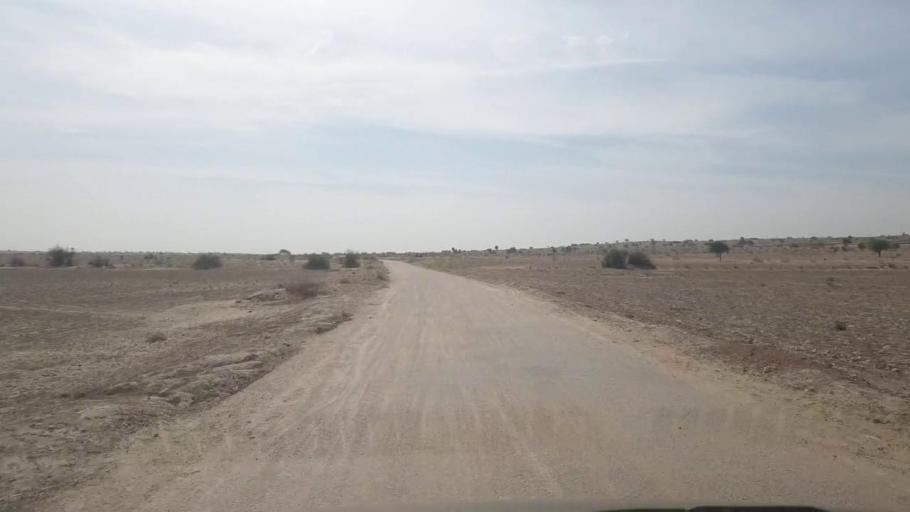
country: PK
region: Sindh
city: Umarkot
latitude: 25.2803
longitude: 69.7288
